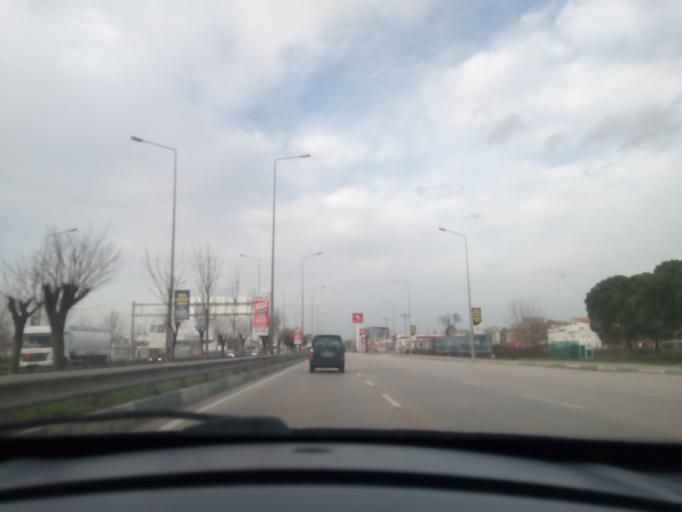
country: TR
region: Bursa
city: Cali
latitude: 40.2139
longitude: 28.9132
